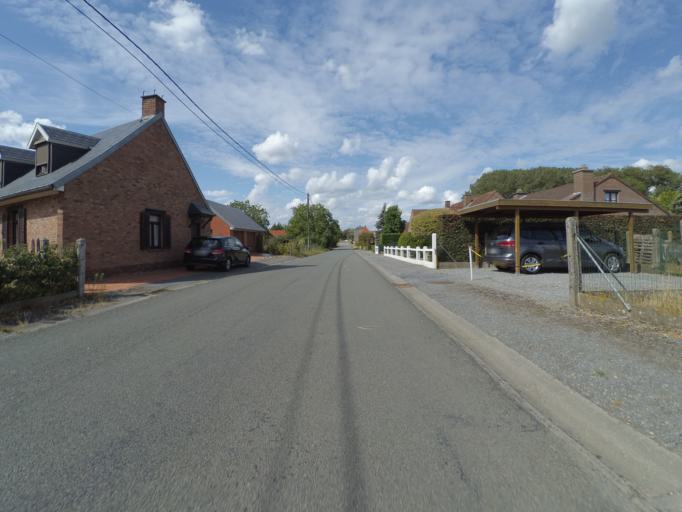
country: BE
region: Flanders
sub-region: Provincie Oost-Vlaanderen
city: Ronse
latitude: 50.7309
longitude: 3.5986
